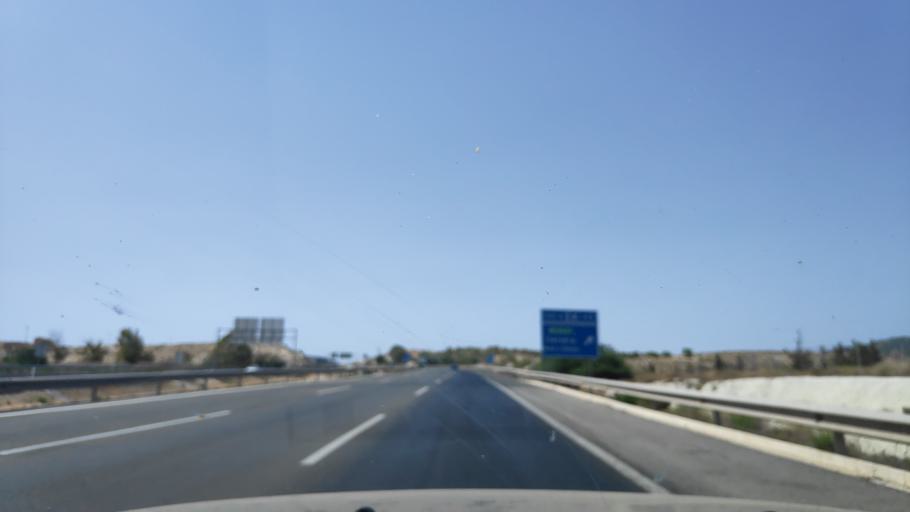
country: ES
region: Murcia
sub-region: Murcia
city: Murcia
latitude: 37.8771
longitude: -1.1297
